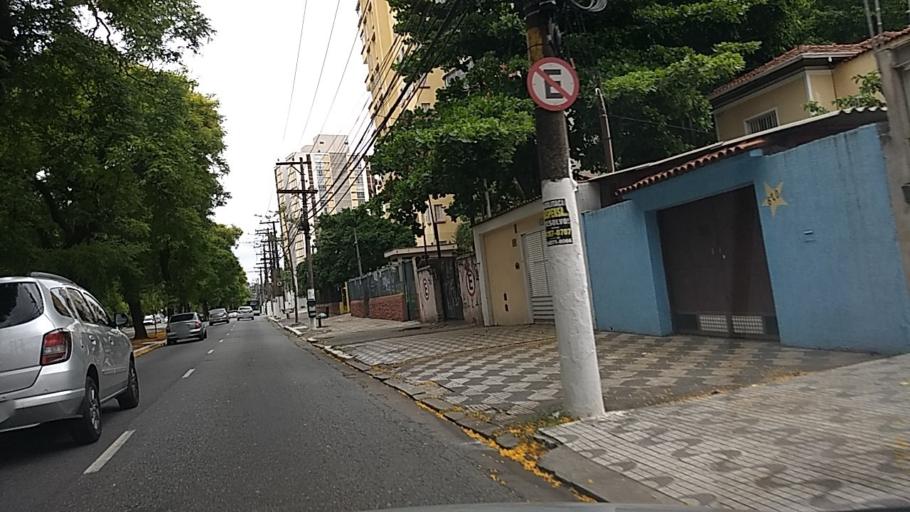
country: BR
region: Sao Paulo
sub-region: Sao Paulo
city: Sao Paulo
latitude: -23.5712
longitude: -46.6112
